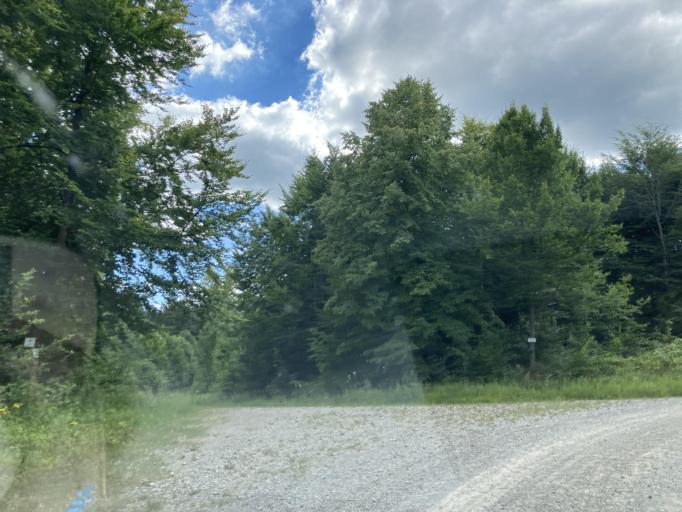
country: DE
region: Baden-Wuerttemberg
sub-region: Tuebingen Region
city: Ofterdingen
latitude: 48.4394
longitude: 9.0161
